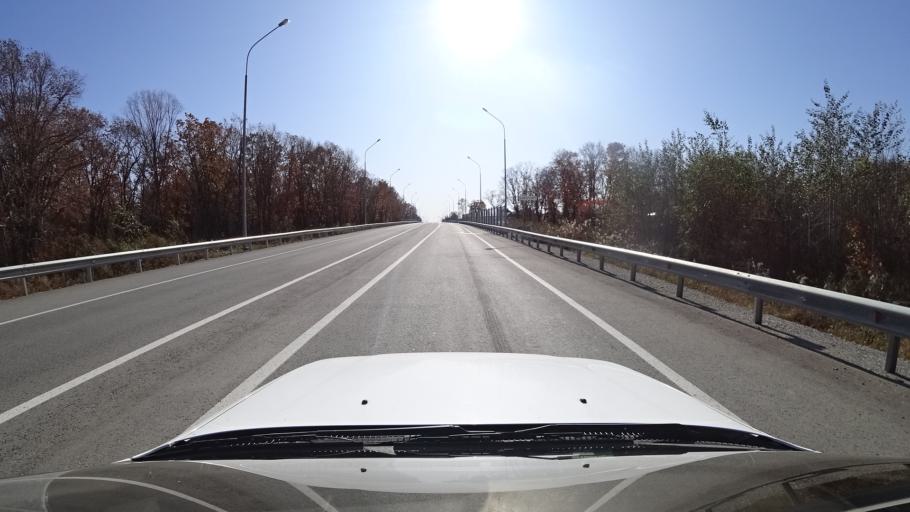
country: RU
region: Primorskiy
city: Dal'nerechensk
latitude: 45.8842
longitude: 133.7301
